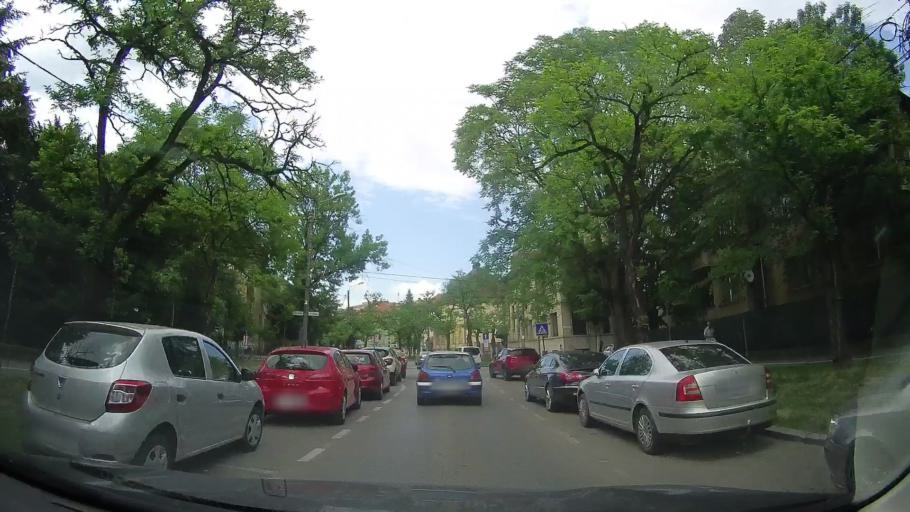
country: RO
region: Timis
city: Timisoara
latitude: 45.7543
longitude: 21.2364
